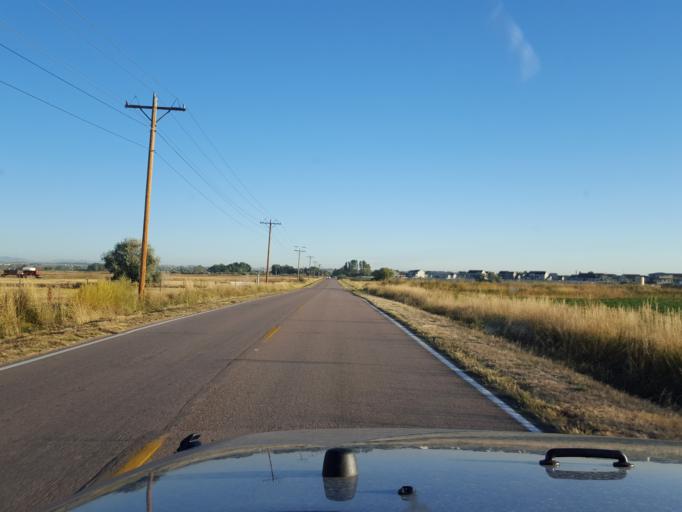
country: US
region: Colorado
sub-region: Weld County
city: Firestone
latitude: 40.1262
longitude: -104.9988
